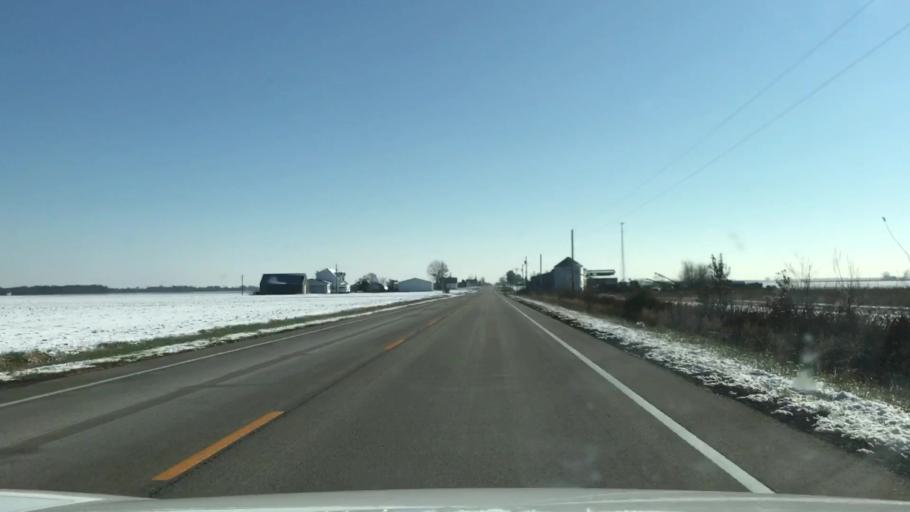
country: US
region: Illinois
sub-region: Washington County
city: Okawville
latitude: 38.4426
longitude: -89.5087
